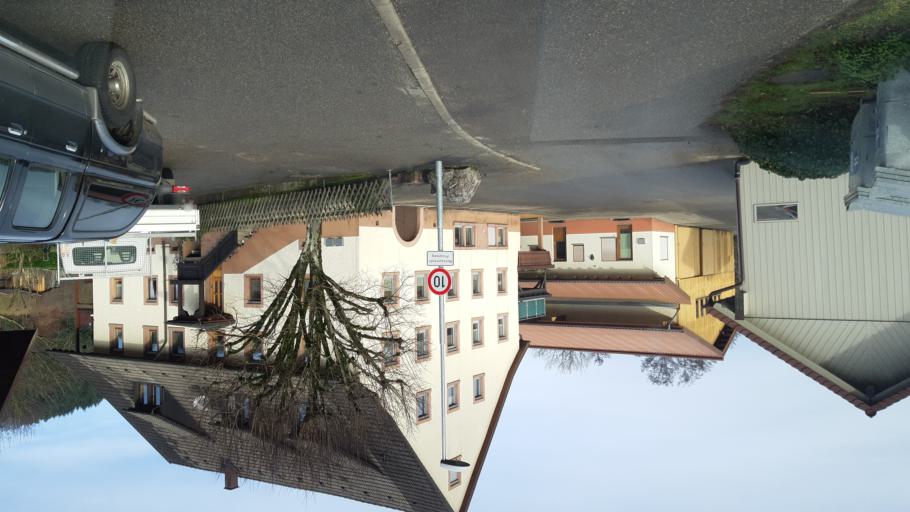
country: DE
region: Baden-Wuerttemberg
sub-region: Freiburg Region
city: Elzach
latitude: 48.1501
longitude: 8.0397
